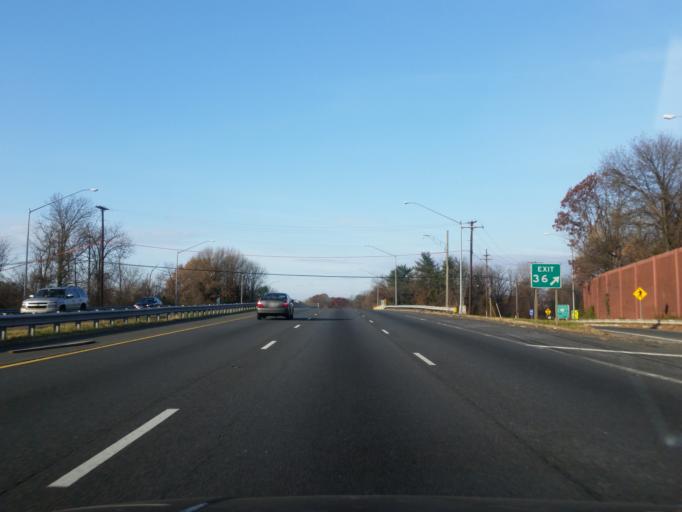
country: US
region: Maryland
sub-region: Montgomery County
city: North Bethesda
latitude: 39.0160
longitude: -77.1171
